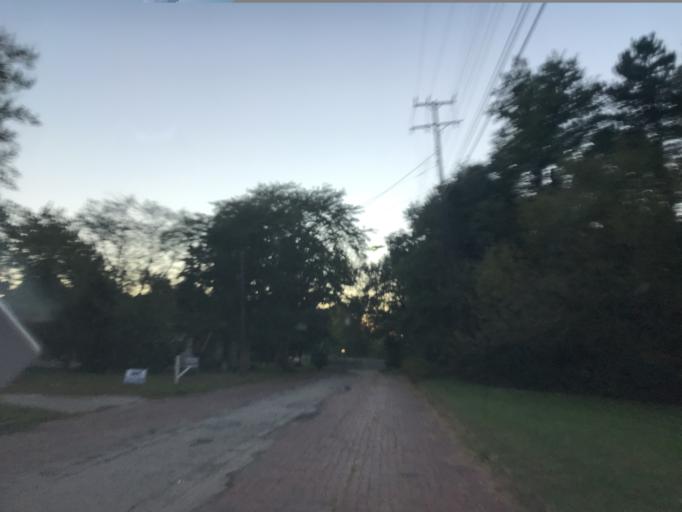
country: US
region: Ohio
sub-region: Ashtabula County
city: Geneva
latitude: 41.7997
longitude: -80.9653
